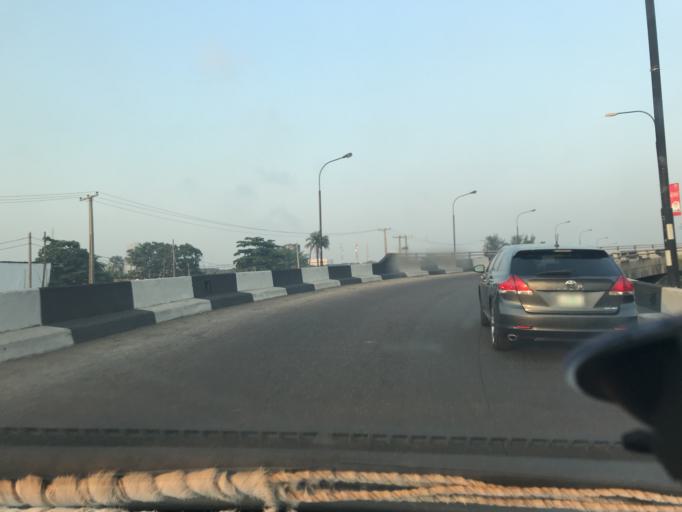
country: NG
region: Lagos
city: Lagos
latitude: 6.4547
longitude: 3.4078
